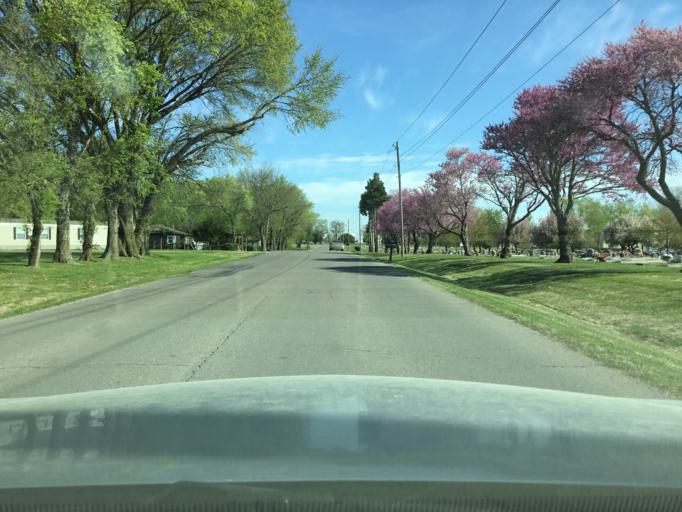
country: US
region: Kansas
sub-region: Neosho County
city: Chanute
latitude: 37.6643
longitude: -95.4434
